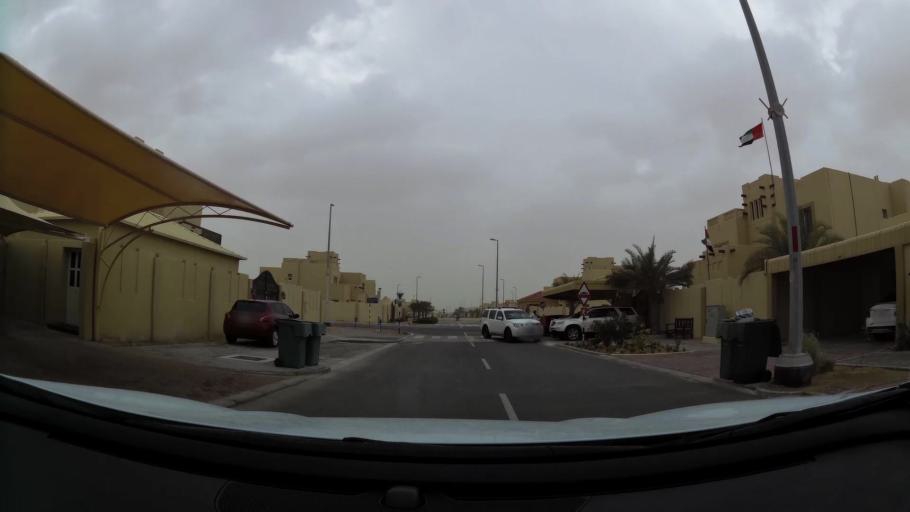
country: AE
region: Abu Dhabi
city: Abu Dhabi
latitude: 24.4551
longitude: 54.7111
